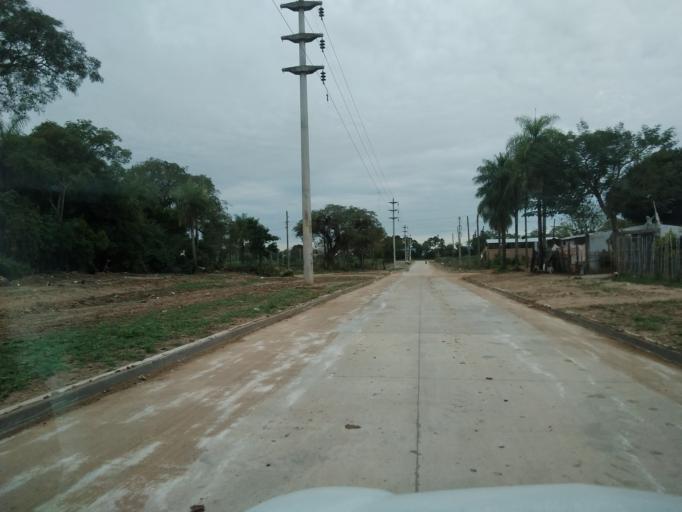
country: AR
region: Corrientes
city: Corrientes
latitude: -27.5148
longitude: -58.8214
